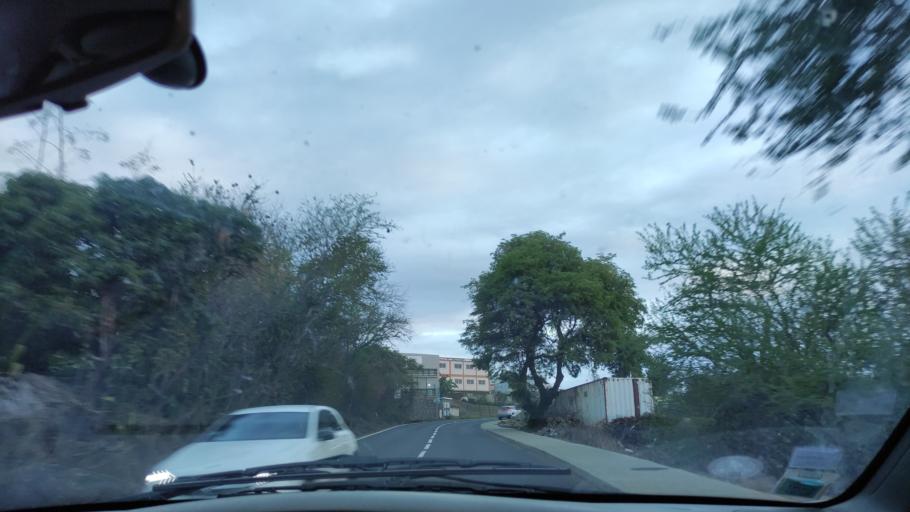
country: RE
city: Piton Saint-Leu
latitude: -21.2087
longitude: 55.2980
